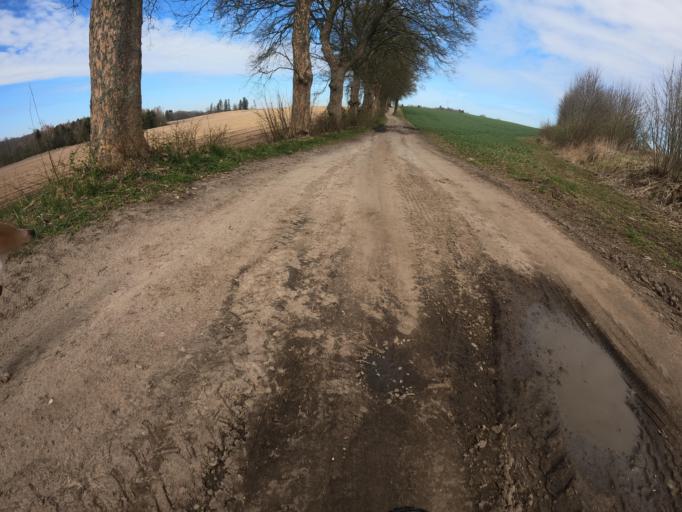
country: PL
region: West Pomeranian Voivodeship
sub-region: Powiat gryficki
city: Brojce
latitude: 53.9644
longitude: 15.3750
